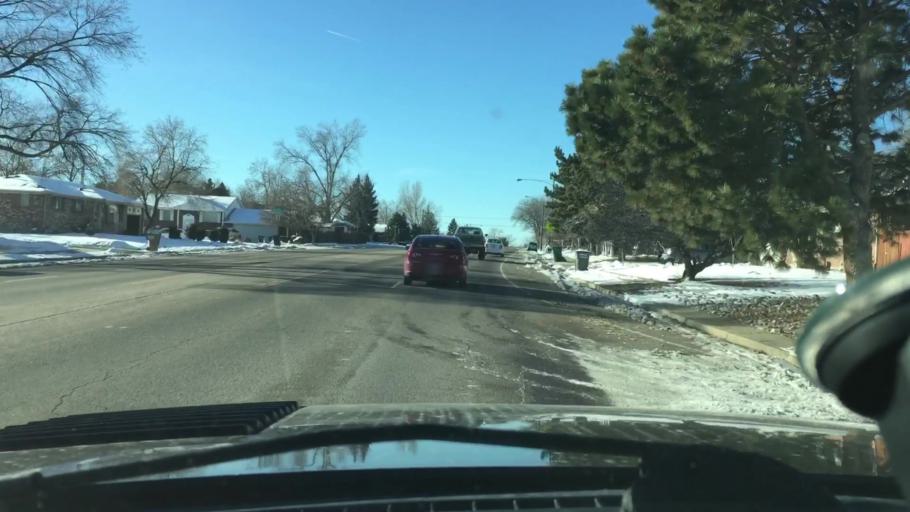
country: US
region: Colorado
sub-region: Adams County
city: Federal Heights
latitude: 39.8467
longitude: -104.9970
